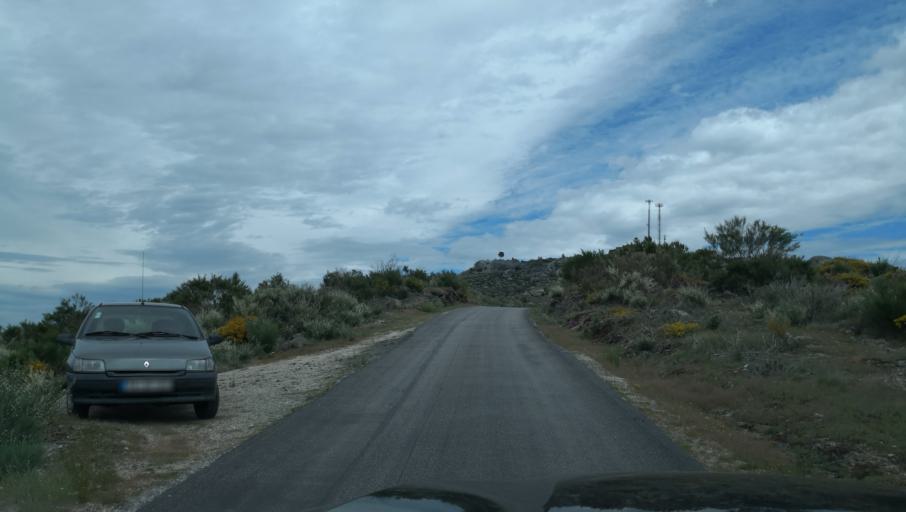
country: PT
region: Vila Real
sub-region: Vila Real
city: Vila Real
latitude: 41.3726
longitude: -7.6960
